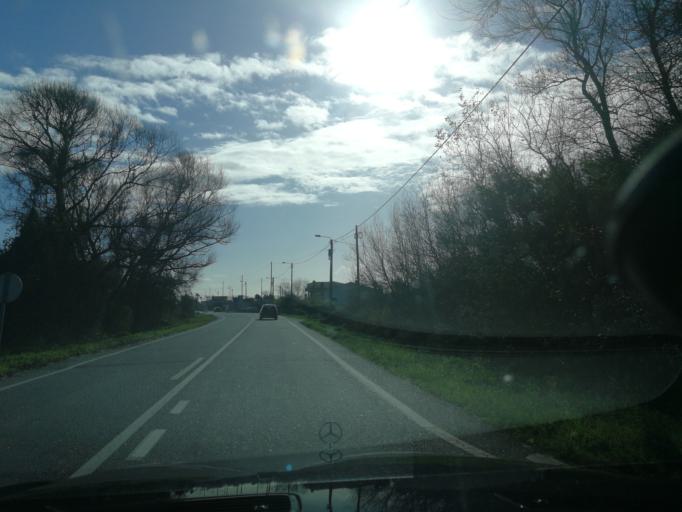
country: PT
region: Aveiro
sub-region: Estarreja
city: Pardilho
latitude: 40.8203
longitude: -8.6693
